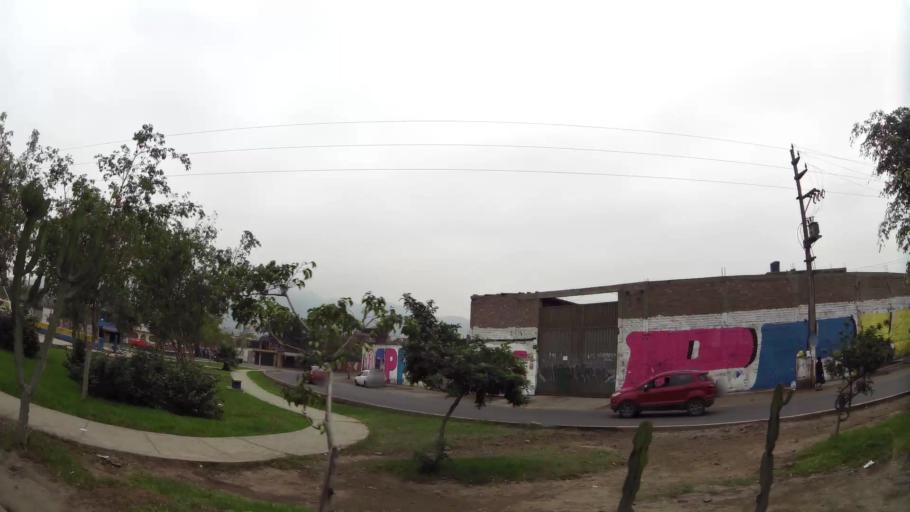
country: PE
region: Lima
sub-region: Lima
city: Independencia
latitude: -11.9879
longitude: -76.9961
